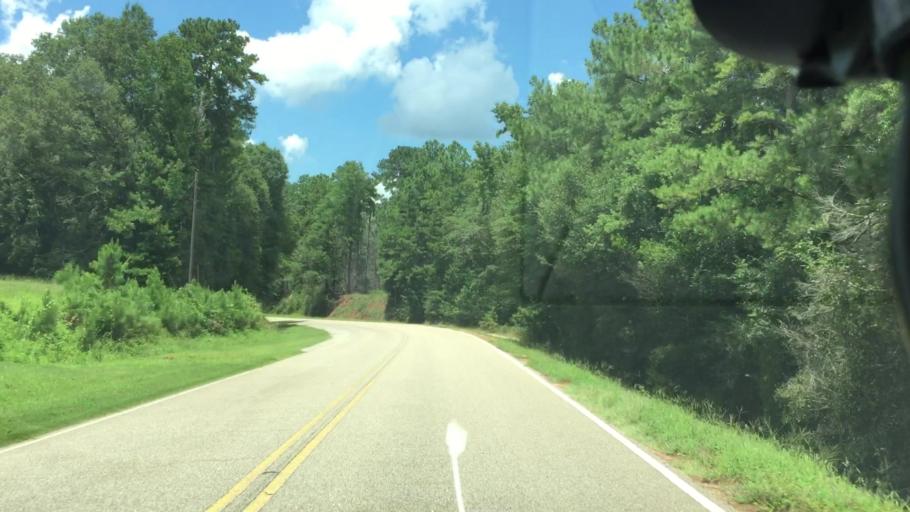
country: US
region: Alabama
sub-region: Coffee County
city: New Brockton
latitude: 31.4073
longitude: -85.8419
